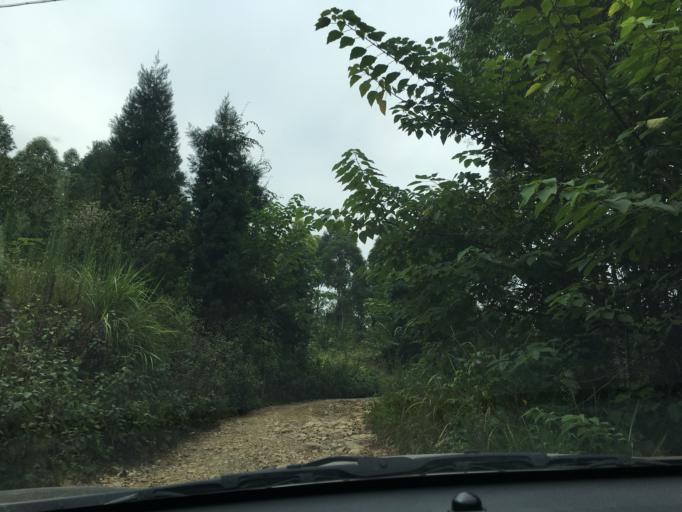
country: CN
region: Guangxi Zhuangzu Zizhiqu
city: Xinzhou
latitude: 25.3798
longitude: 105.6367
